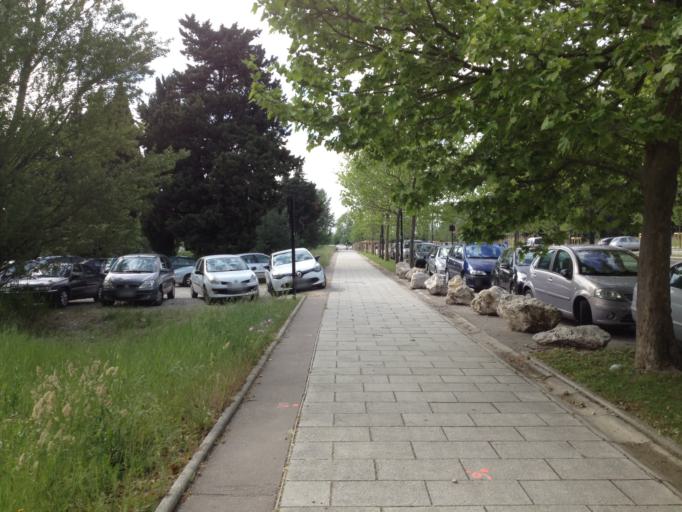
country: FR
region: Provence-Alpes-Cote d'Azur
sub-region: Departement des Bouches-du-Rhone
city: Rognonas
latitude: 43.9260
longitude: 4.7865
